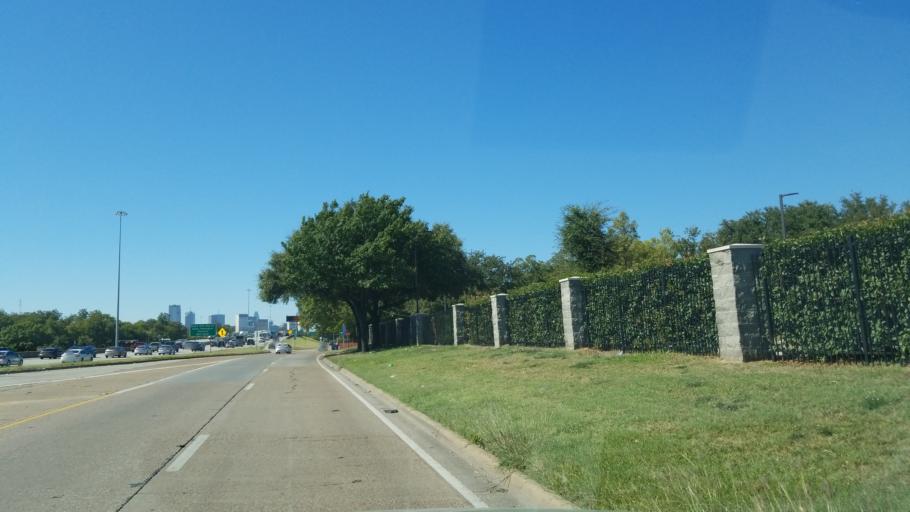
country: US
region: Texas
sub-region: Dallas County
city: Dallas
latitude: 32.7916
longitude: -96.7521
